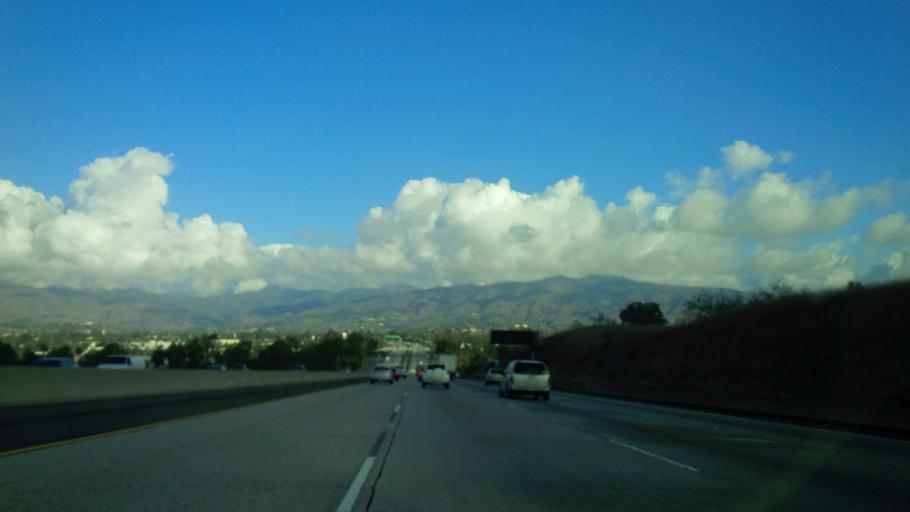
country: US
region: California
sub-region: Los Angeles County
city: San Dimas
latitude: 34.0901
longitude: -117.8194
